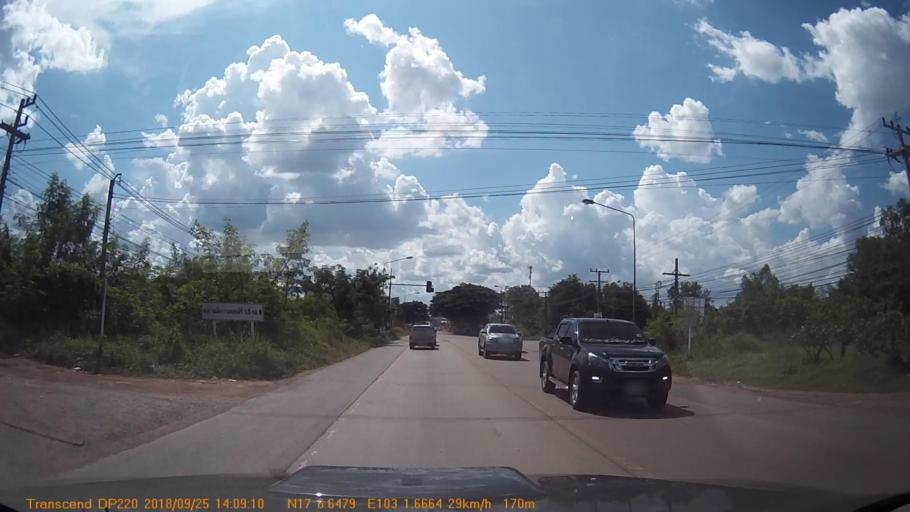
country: TH
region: Changwat Udon Thani
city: Kumphawapi
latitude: 17.1108
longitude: 103.0277
